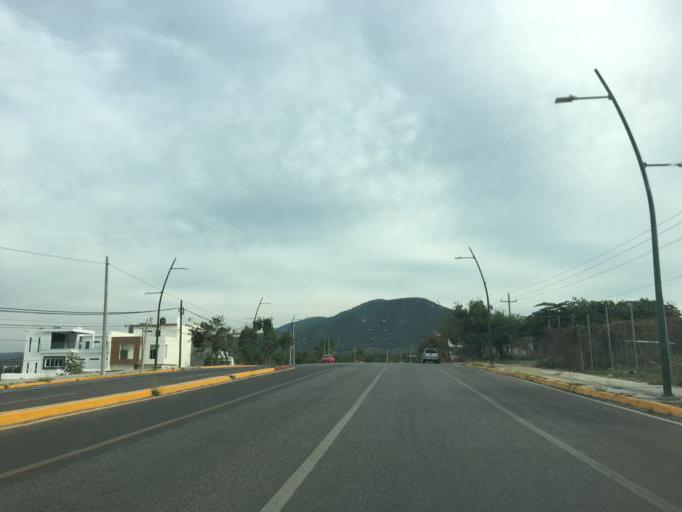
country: MX
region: Chiapas
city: Tuxtla Gutierrez
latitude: 16.7699
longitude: -93.1720
